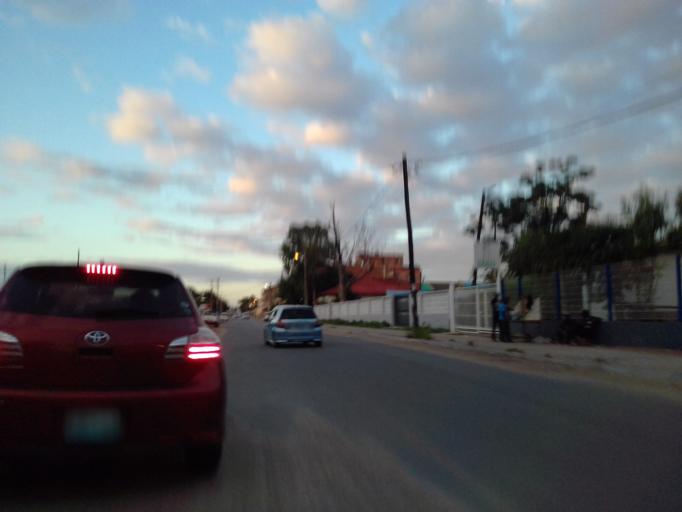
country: MZ
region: Maputo City
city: Maputo
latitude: -25.9558
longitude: 32.5792
